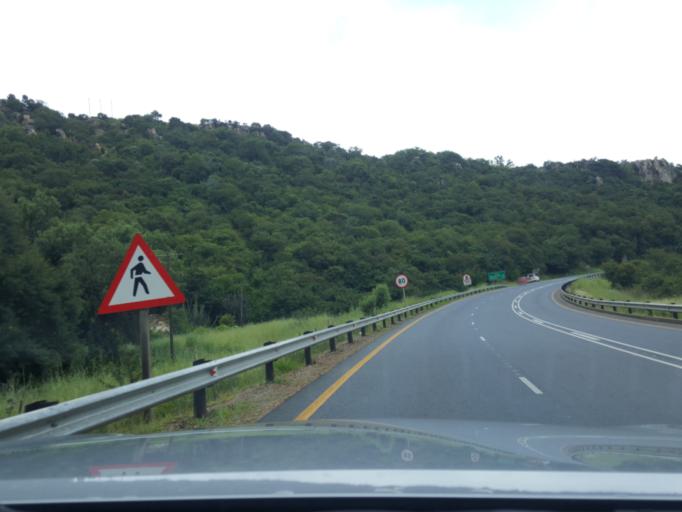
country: ZA
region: Mpumalanga
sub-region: Nkangala District Municipality
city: Belfast
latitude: -25.6441
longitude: 30.3474
